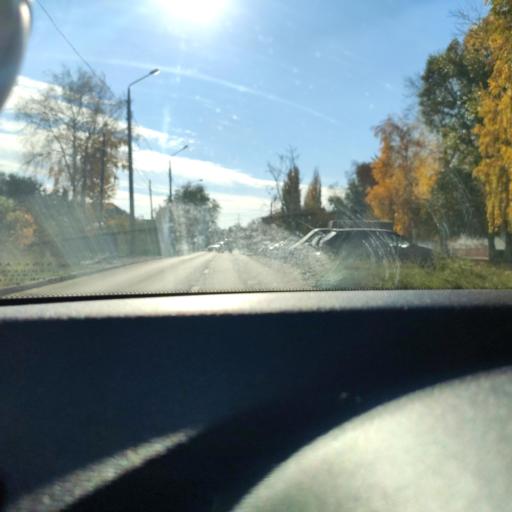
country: RU
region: Samara
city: Petra-Dubrava
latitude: 53.2331
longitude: 50.2991
